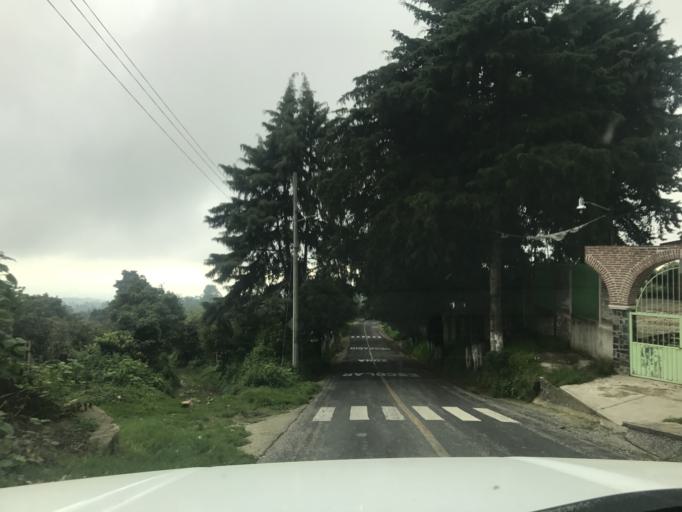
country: MX
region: Morelos
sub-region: Ocuituco
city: Huepalcalco (San Miguel)
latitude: 18.9160
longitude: -98.7446
